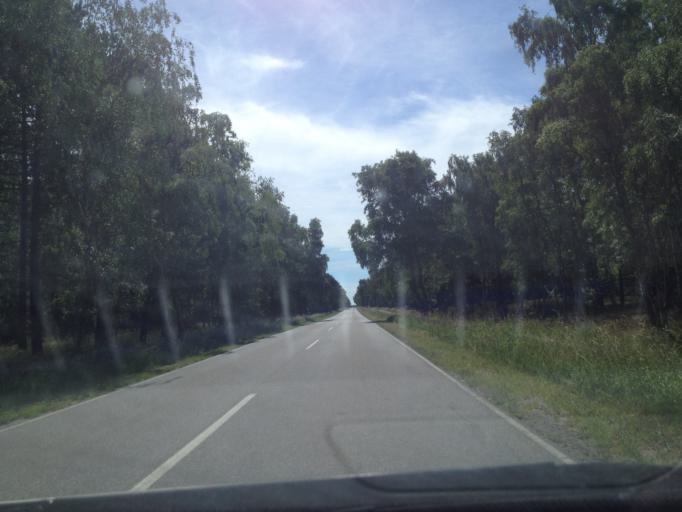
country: DK
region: Central Jutland
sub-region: Samso Kommune
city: Tranebjerg
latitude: 55.9370
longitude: 10.5805
